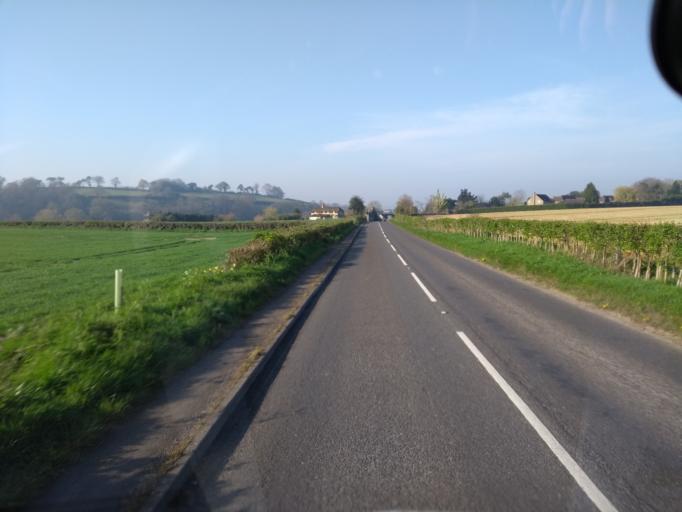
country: GB
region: England
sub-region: Somerset
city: Ilminster
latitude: 50.9290
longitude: -2.8990
